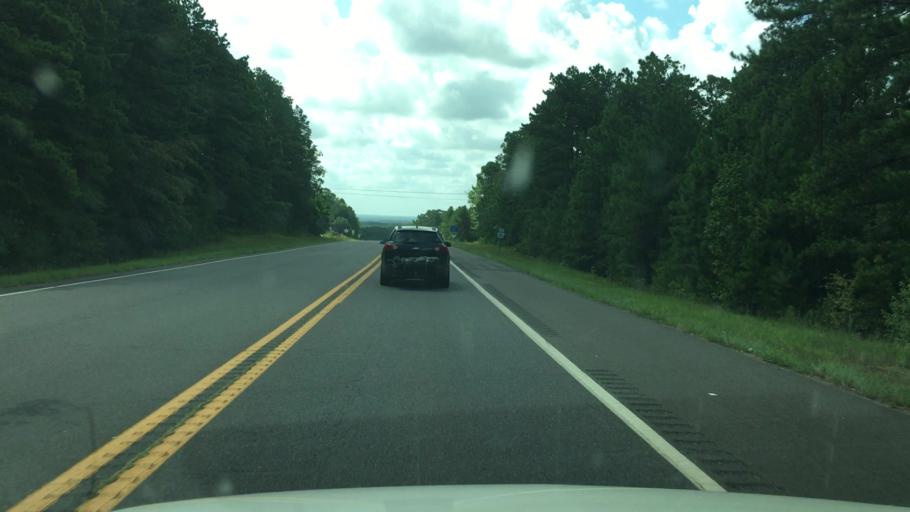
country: US
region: Arkansas
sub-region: Clark County
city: Arkadelphia
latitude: 34.2166
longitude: -93.0854
